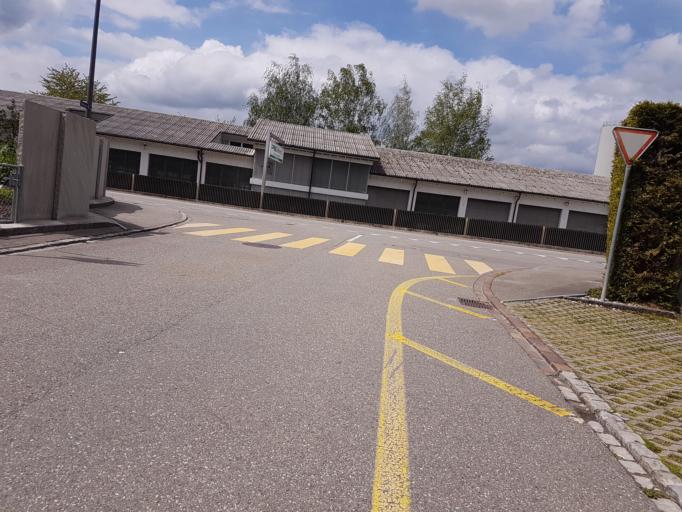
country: CH
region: Aargau
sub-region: Bezirk Brugg
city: Lauffohr (Brugg)
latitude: 47.5185
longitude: 8.2415
